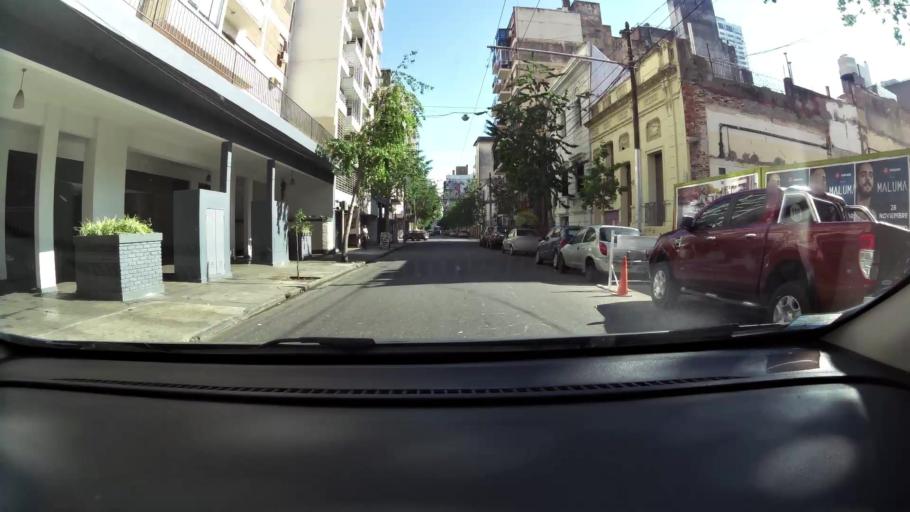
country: AR
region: Santa Fe
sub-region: Departamento de Rosario
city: Rosario
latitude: -32.9524
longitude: -60.6308
